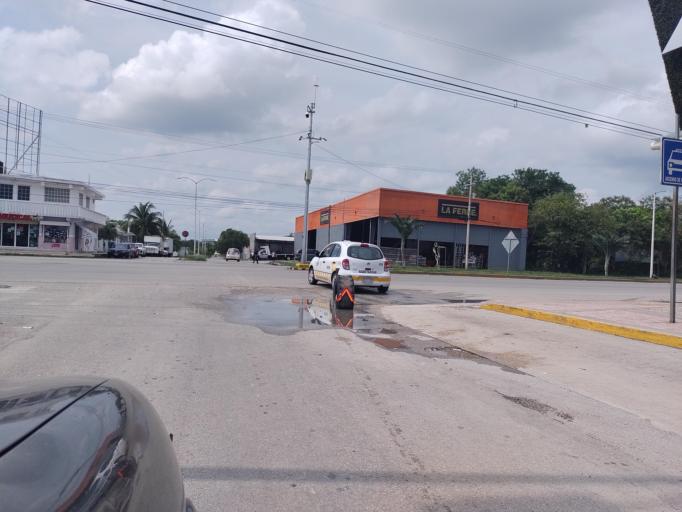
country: MX
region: Quintana Roo
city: Chetumal
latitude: 18.5188
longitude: -88.3137
